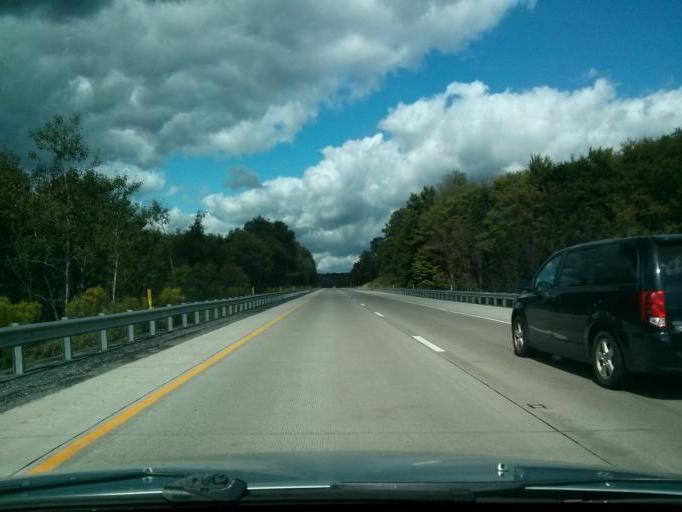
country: US
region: Pennsylvania
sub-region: Jefferson County
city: Falls Creek
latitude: 41.1554
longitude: -78.8135
